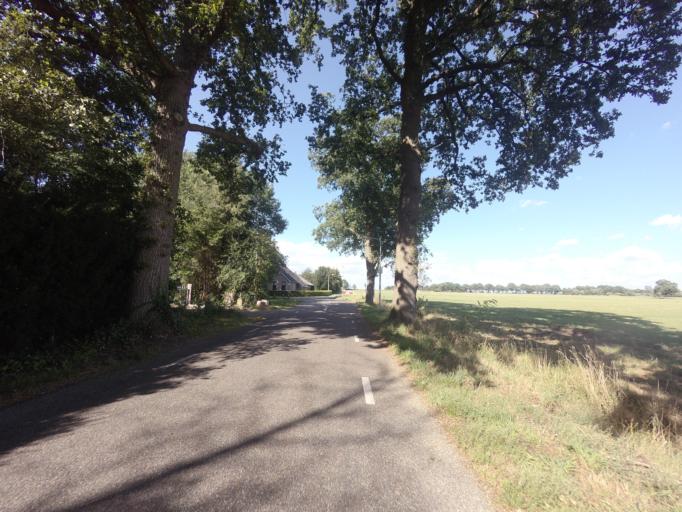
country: NL
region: Drenthe
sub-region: Gemeente Hoogeveen
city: Hoogeveen
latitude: 52.6292
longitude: 6.4837
